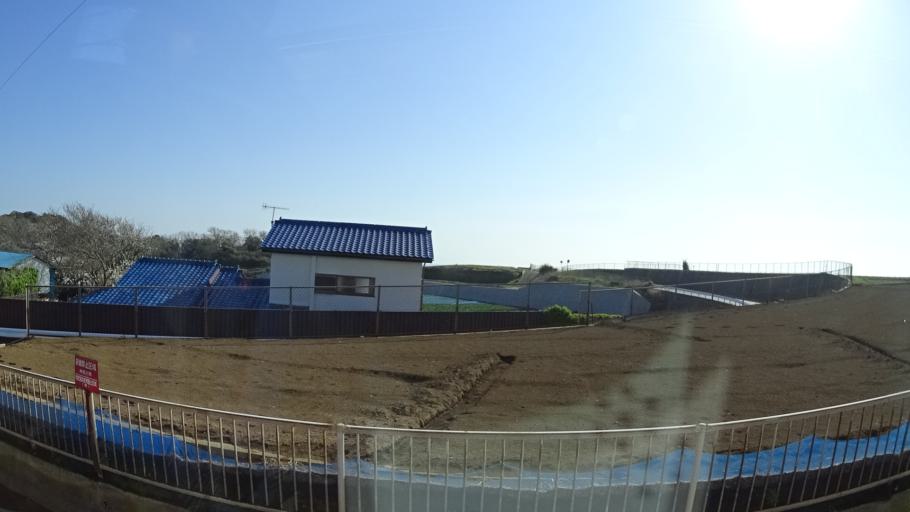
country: JP
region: Kanagawa
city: Miura
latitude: 35.1567
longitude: 139.6435
